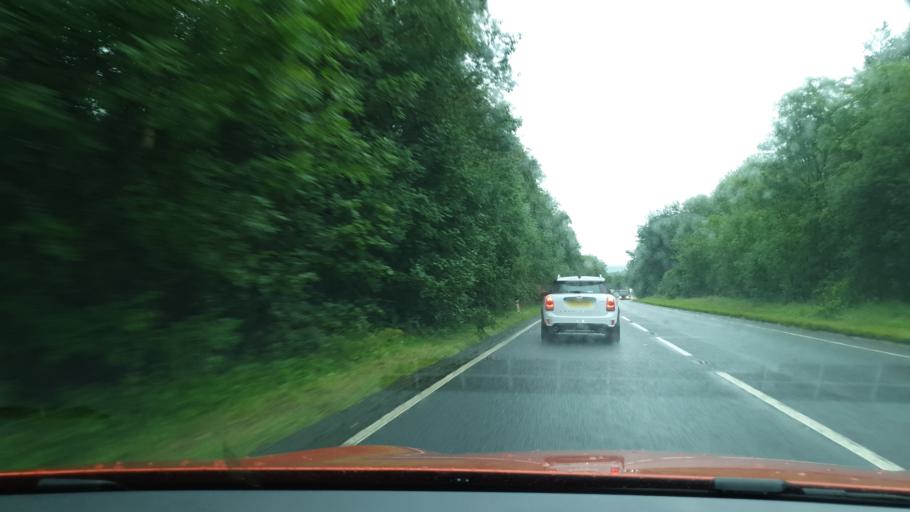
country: GB
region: England
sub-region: Cumbria
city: Ulverston
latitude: 54.2491
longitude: -3.0069
